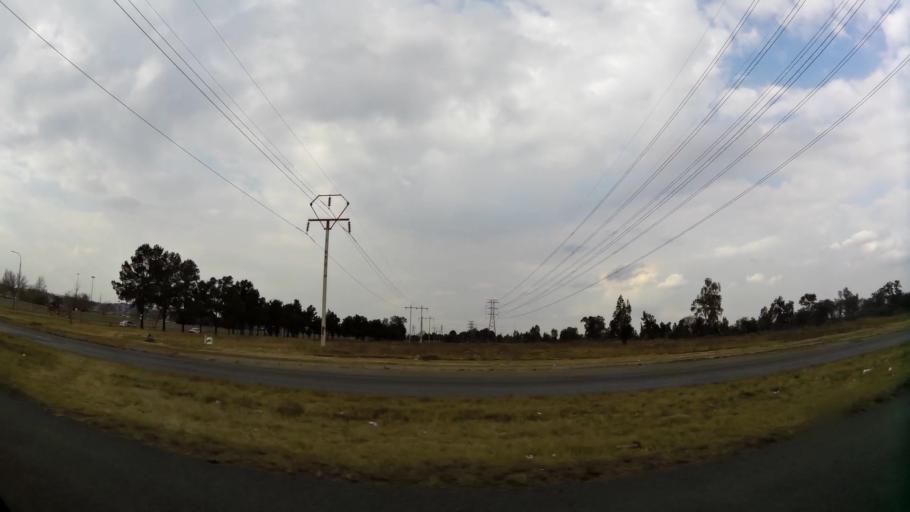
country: ZA
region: Gauteng
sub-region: Sedibeng District Municipality
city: Vanderbijlpark
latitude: -26.6716
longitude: 27.8374
